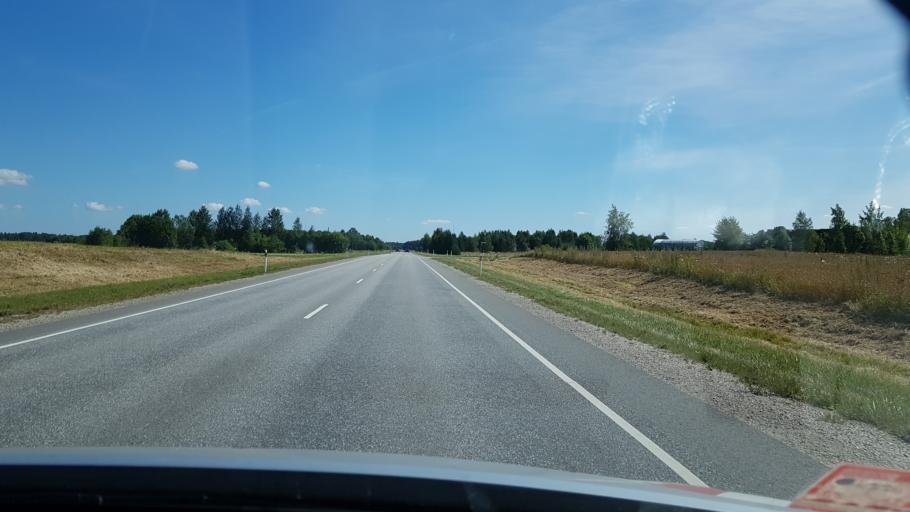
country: EE
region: Tartu
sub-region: Tartu linn
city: Tartu
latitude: 58.3728
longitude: 26.8405
